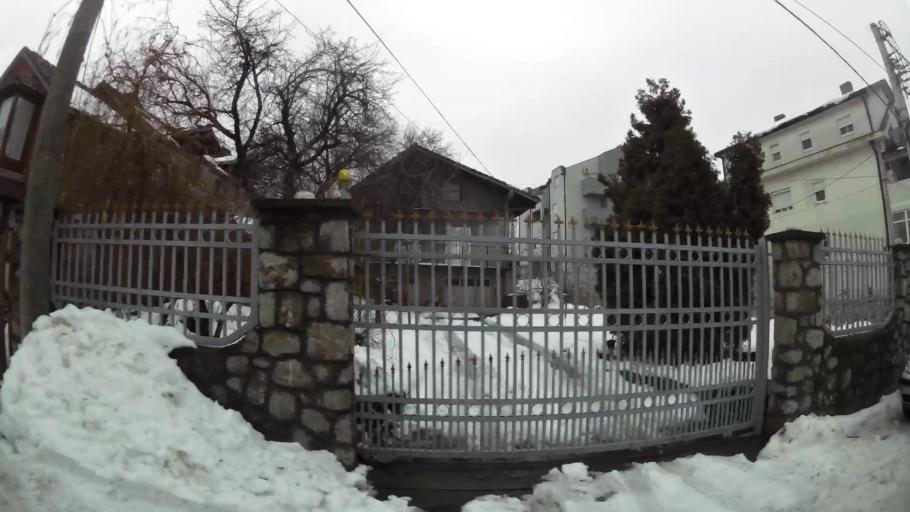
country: RS
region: Central Serbia
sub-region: Belgrade
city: Zvezdara
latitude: 44.7407
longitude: 20.5037
